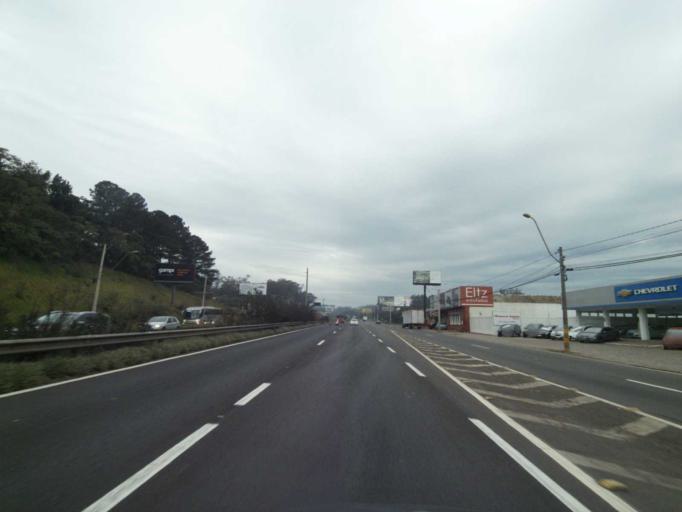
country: BR
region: Rio Grande do Sul
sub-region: Sao Leopoldo
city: Sao Leopoldo
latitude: -29.7815
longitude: -51.1595
